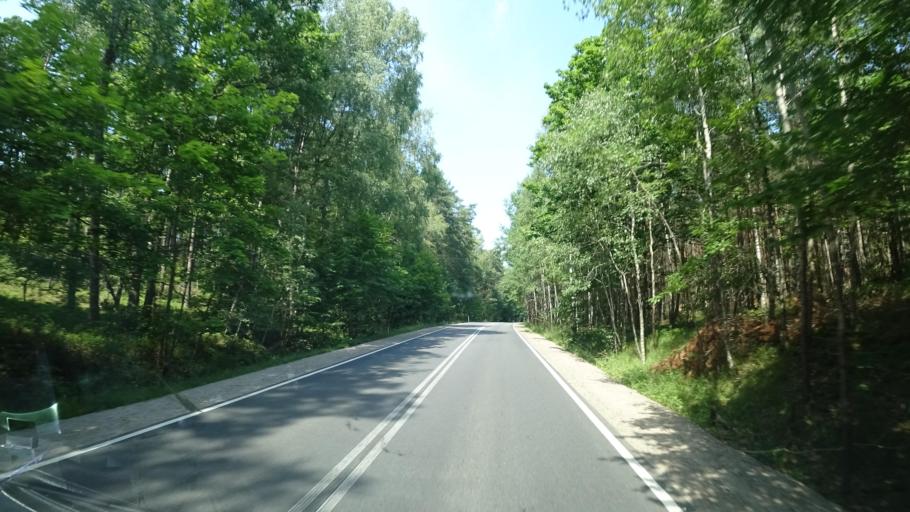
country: PL
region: Pomeranian Voivodeship
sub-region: Powiat koscierski
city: Dziemiany
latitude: 53.9845
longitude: 17.7730
